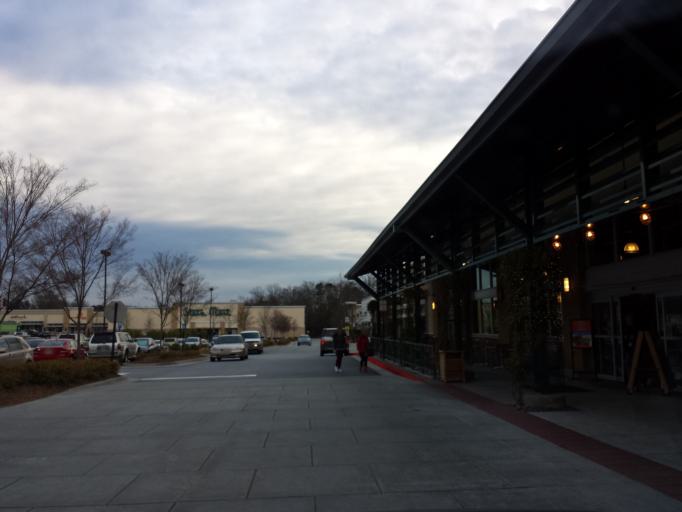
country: US
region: Georgia
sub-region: Fulton County
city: Sandy Springs
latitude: 33.9809
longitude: -84.4274
